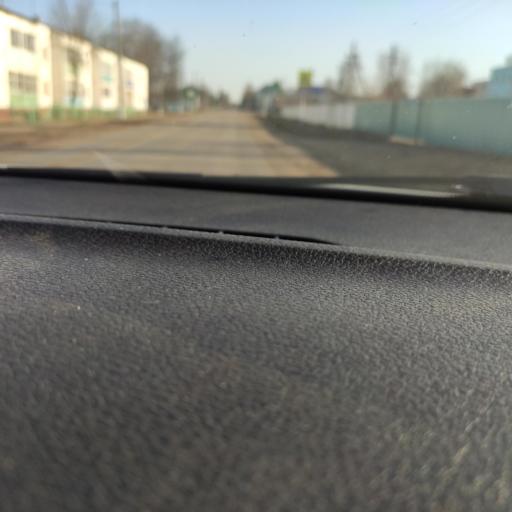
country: RU
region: Bashkortostan
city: Ulukulevo
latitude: 54.3780
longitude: 56.4495
